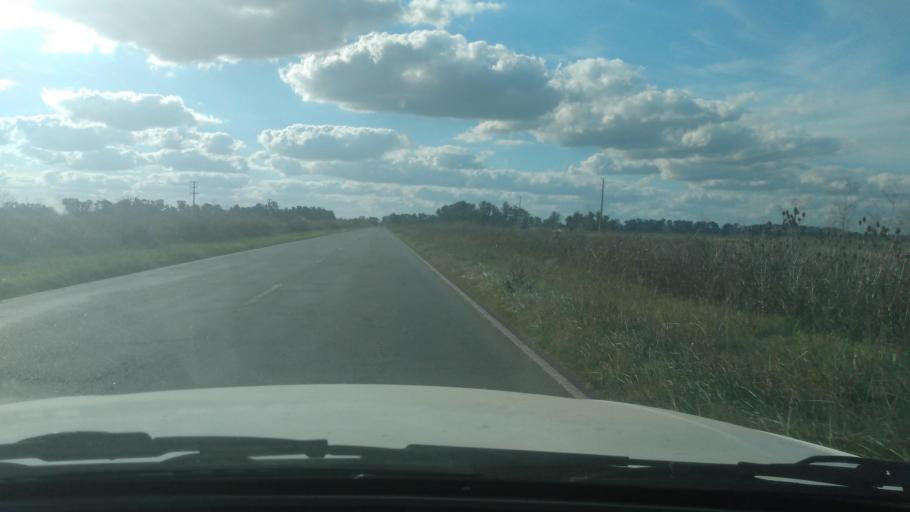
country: AR
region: Buenos Aires
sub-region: Partido de Mercedes
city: Mercedes
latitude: -34.7287
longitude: -59.3909
